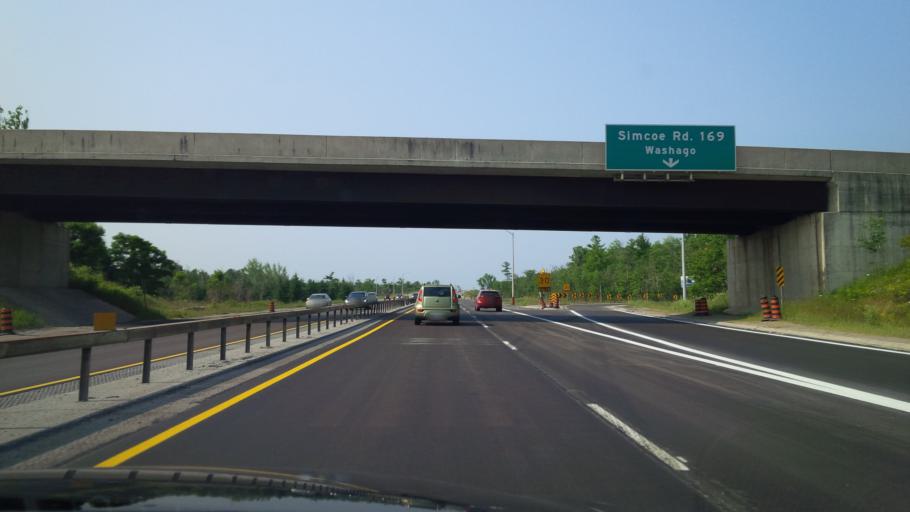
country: CA
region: Ontario
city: Gravenhurst
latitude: 44.7571
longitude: -79.3375
